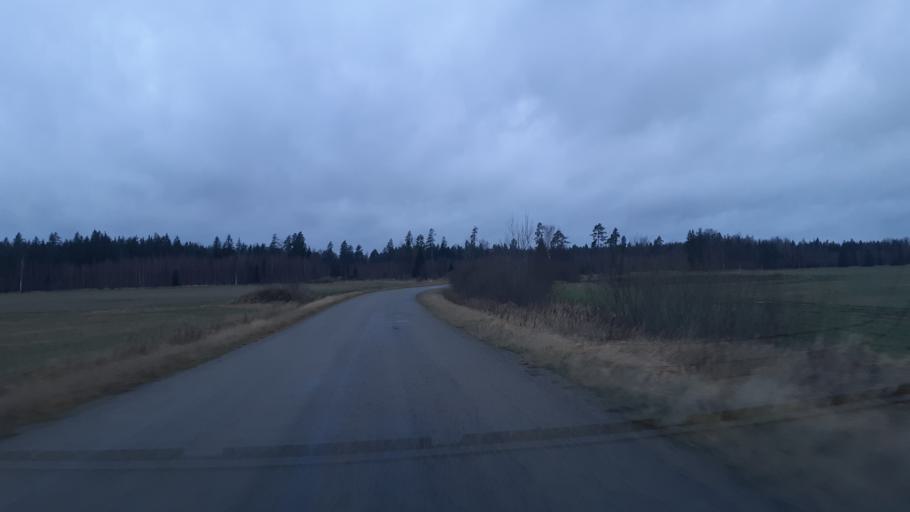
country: LV
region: Kuldigas Rajons
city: Kuldiga
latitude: 57.0289
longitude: 22.1610
